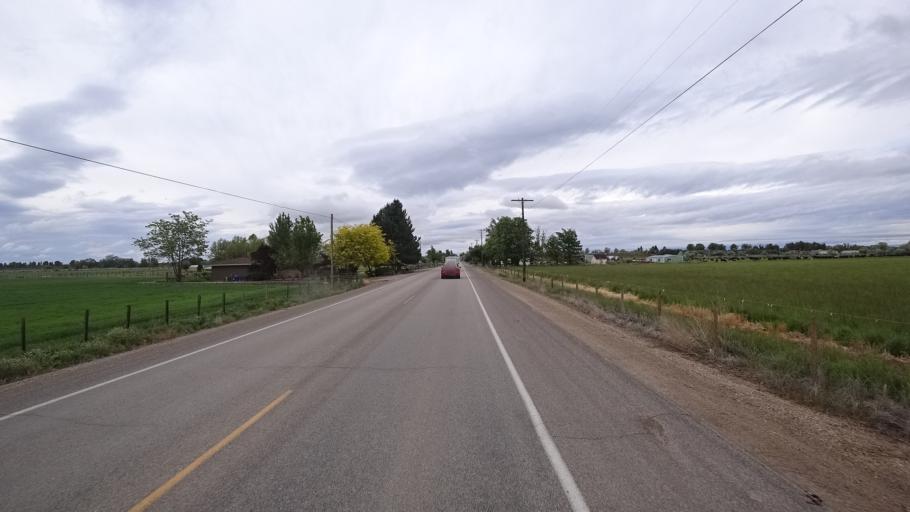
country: US
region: Idaho
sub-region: Ada County
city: Star
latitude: 43.6750
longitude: -116.4934
